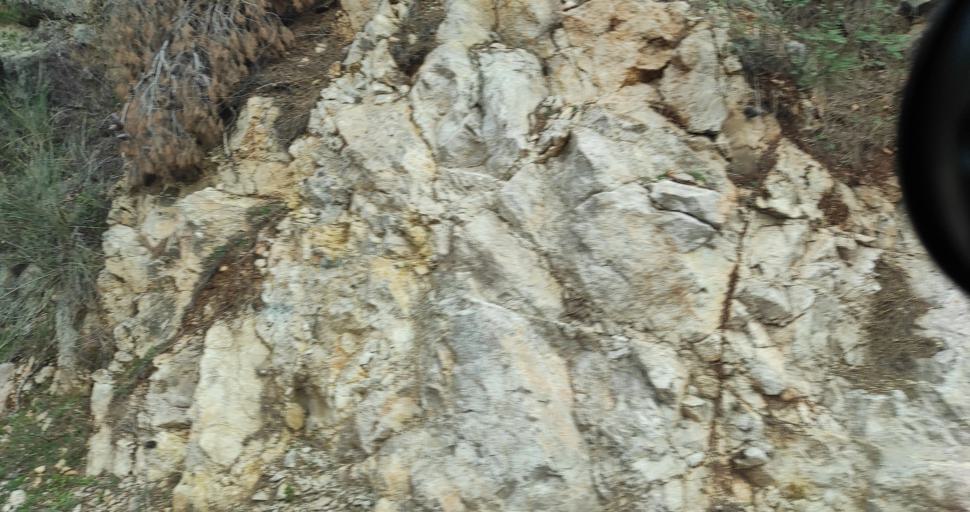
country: AL
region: Lezhe
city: Shengjin
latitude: 41.8160
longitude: 19.5687
